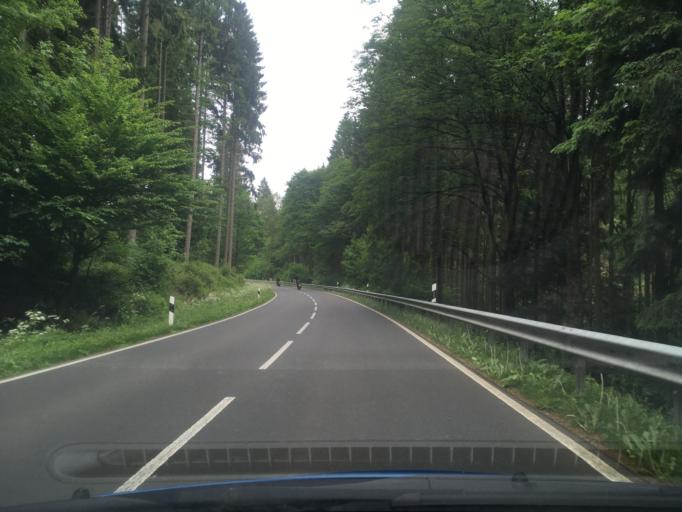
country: DE
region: Lower Saxony
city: Dassel
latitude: 51.7572
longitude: 9.6776
